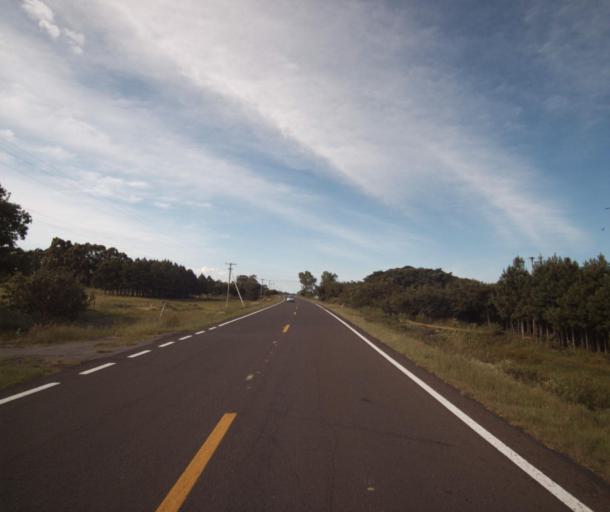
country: BR
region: Rio Grande do Sul
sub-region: Tapes
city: Tapes
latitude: -31.3265
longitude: -51.1258
